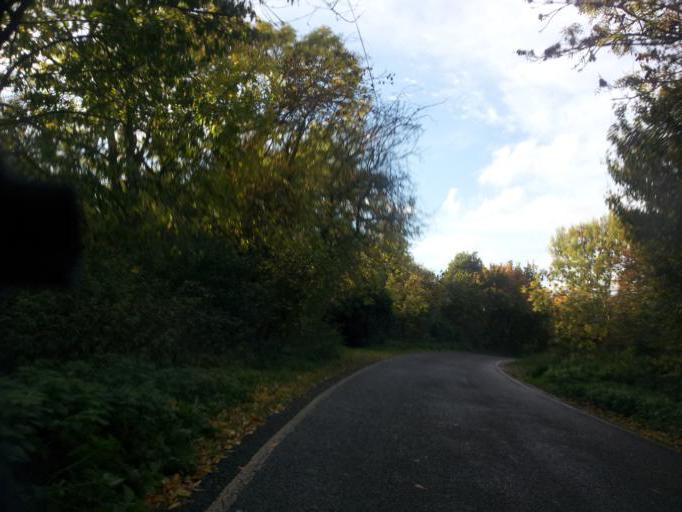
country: GB
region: England
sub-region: Kent
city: Sittingbourne
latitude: 51.3732
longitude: 0.7123
